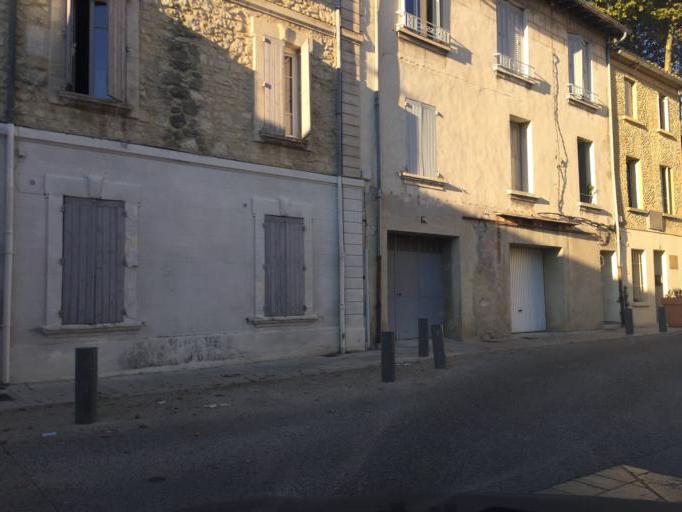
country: FR
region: Provence-Alpes-Cote d'Azur
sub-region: Departement du Vaucluse
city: Avignon
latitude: 43.9504
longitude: 4.8169
